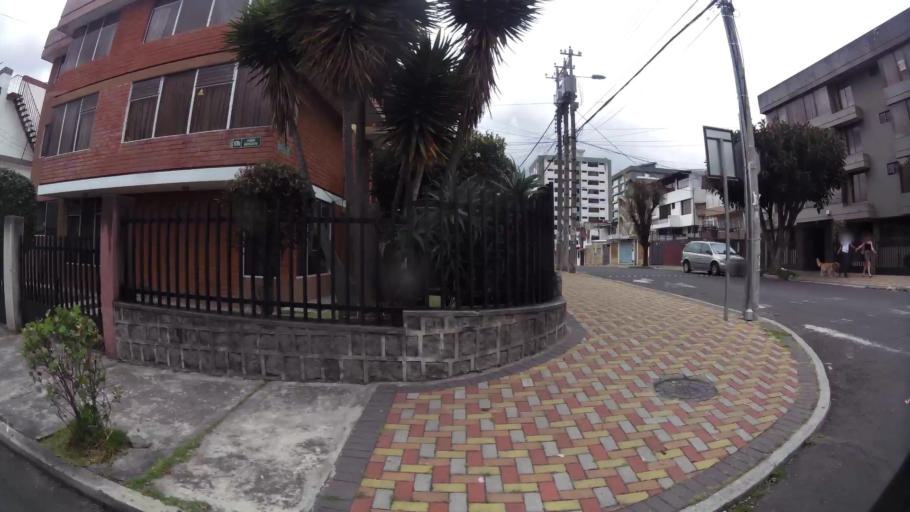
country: EC
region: Pichincha
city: Quito
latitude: -0.1728
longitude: -78.4742
